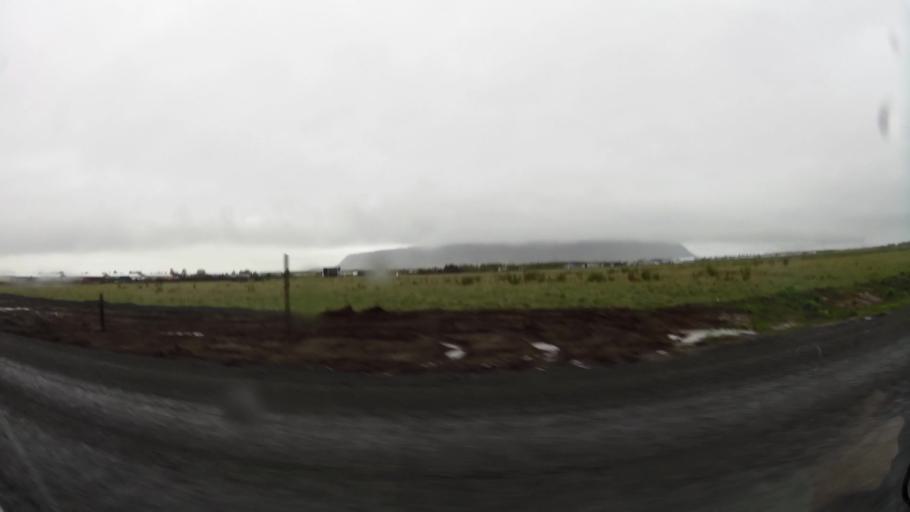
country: IS
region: South
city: Selfoss
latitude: 63.9271
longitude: -20.9726
